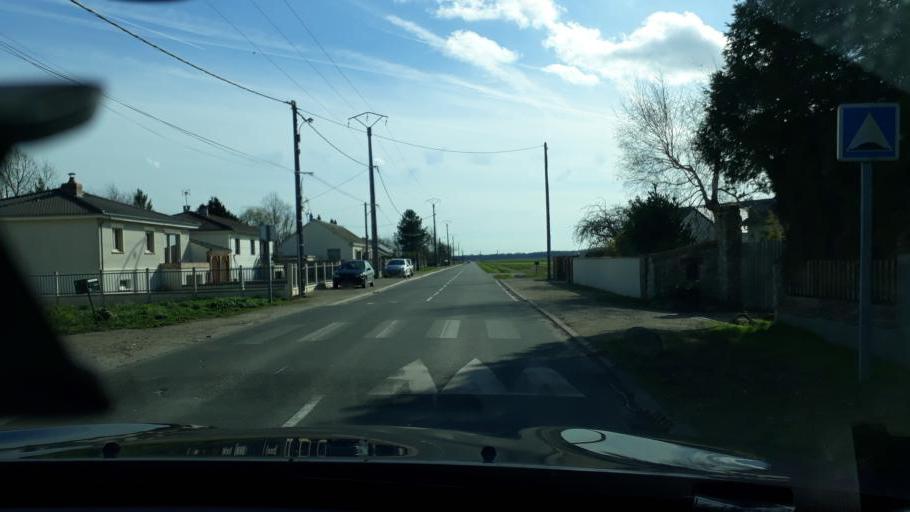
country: FR
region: Centre
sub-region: Departement du Loiret
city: Ascheres-le-Marche
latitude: 48.0662
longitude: 1.9950
